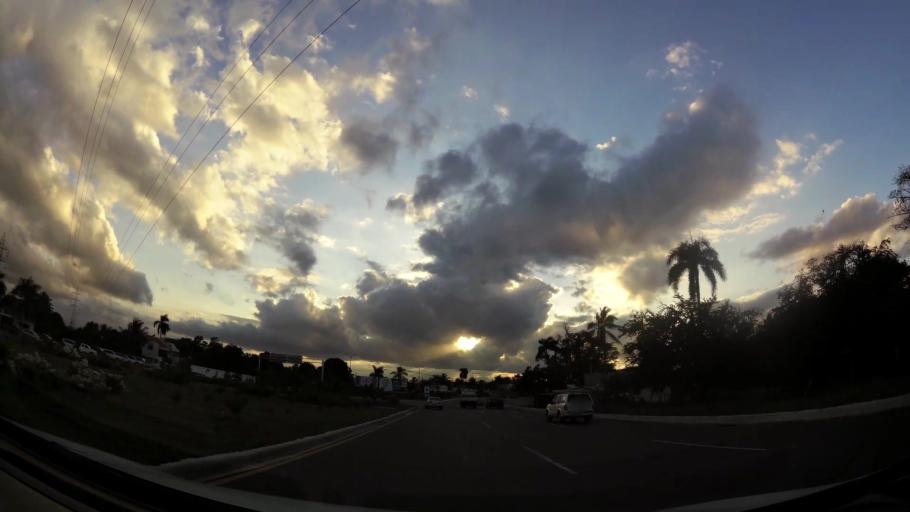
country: DO
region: Santiago
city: Licey al Medio
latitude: 19.4129
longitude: -70.6463
